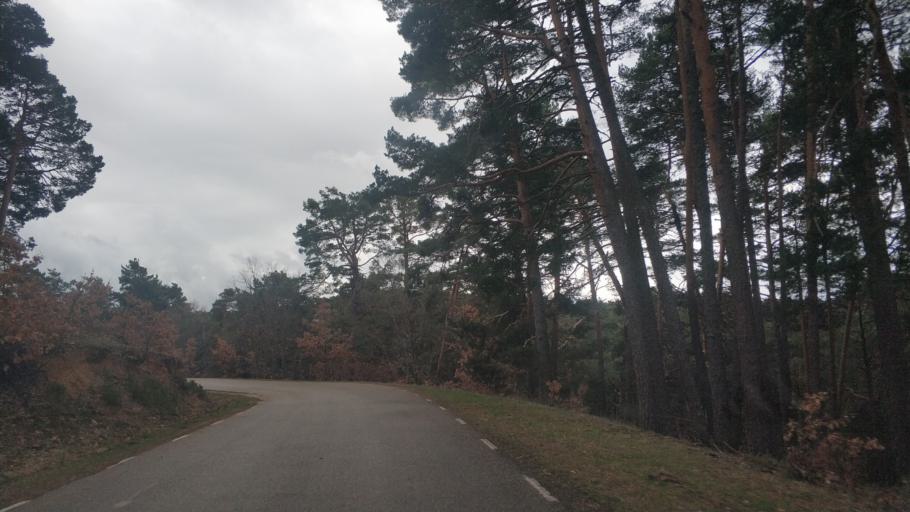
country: ES
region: Castille and Leon
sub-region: Provincia de Burgos
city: Canicosa de la Sierra
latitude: 41.9233
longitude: -3.0393
